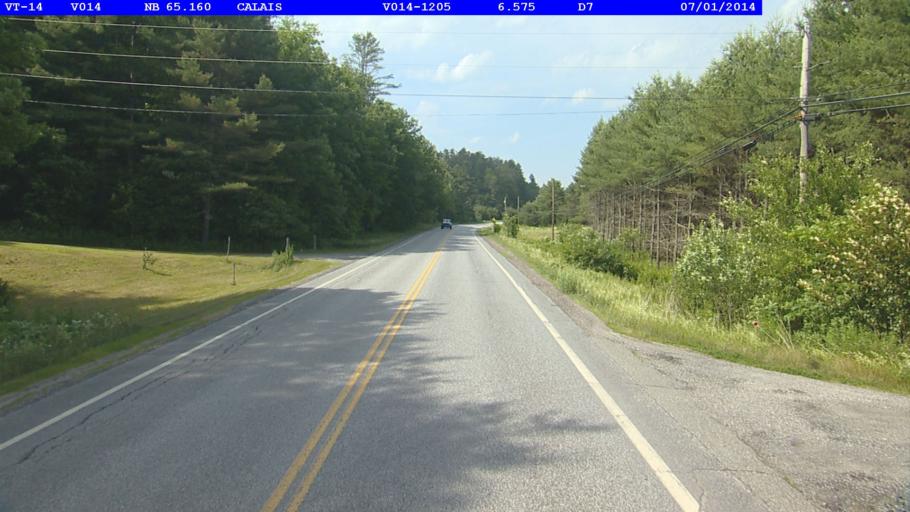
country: US
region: Vermont
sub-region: Caledonia County
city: Hardwick
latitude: 44.3916
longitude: -72.4146
